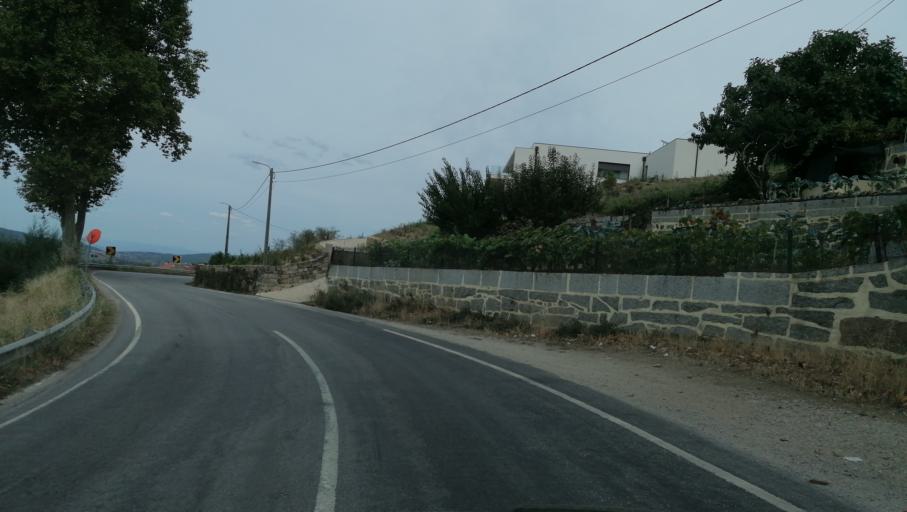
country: PT
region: Vila Real
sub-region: Vila Pouca de Aguiar
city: Vila Pouca de Aguiar
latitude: 41.5146
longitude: -7.6228
